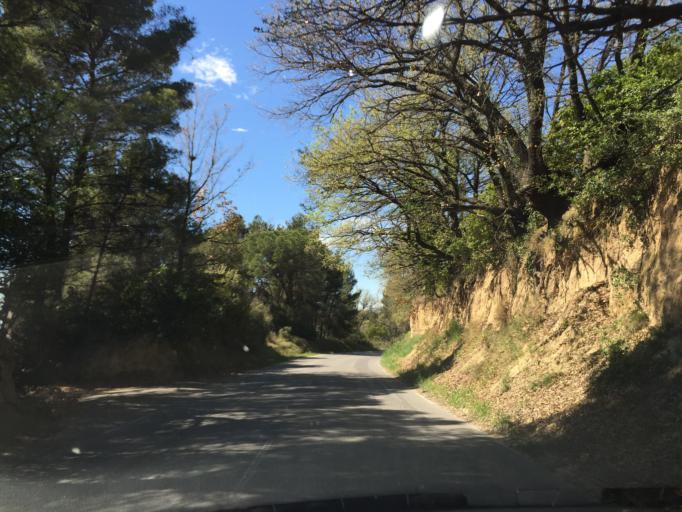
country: FR
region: Provence-Alpes-Cote d'Azur
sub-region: Departement du Vaucluse
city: Cadenet
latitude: 43.7382
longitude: 5.3521
